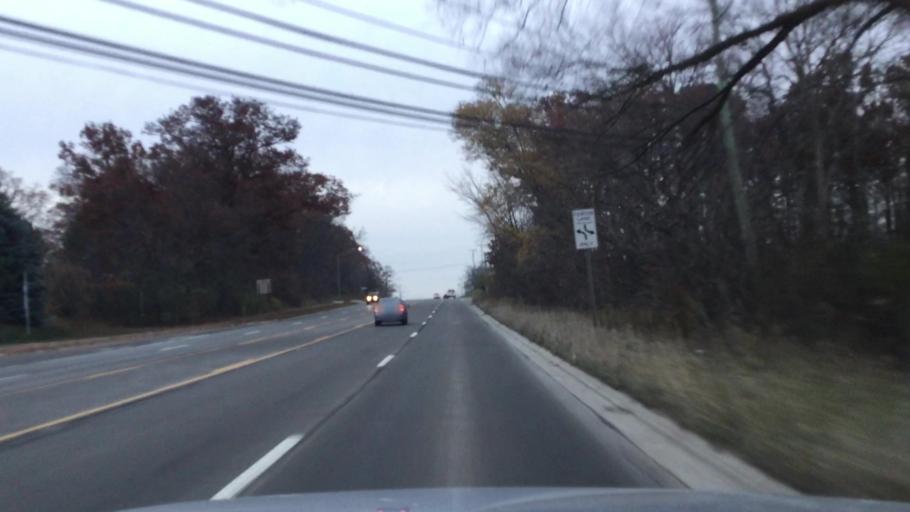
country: US
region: Michigan
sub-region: Oakland County
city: Pontiac
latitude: 42.6312
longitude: -83.2495
